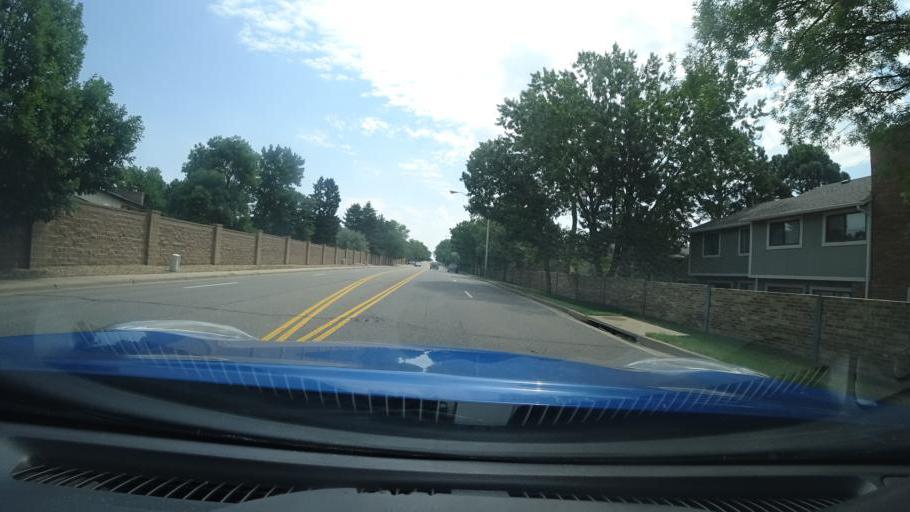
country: US
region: Colorado
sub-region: Adams County
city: Aurora
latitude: 39.6676
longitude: -104.8592
